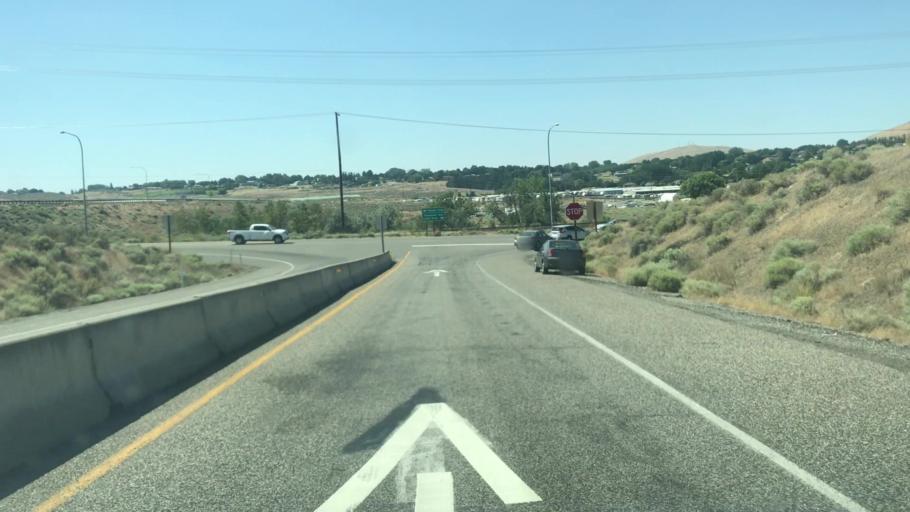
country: US
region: Washington
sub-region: Benton County
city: Richland
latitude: 46.1948
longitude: -119.2659
